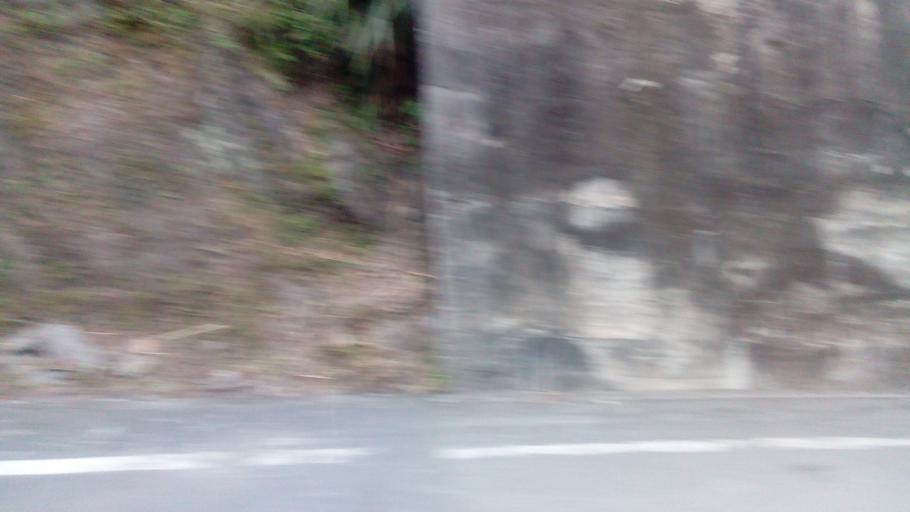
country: TW
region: Taiwan
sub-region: Yilan
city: Yilan
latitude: 24.5650
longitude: 121.4741
